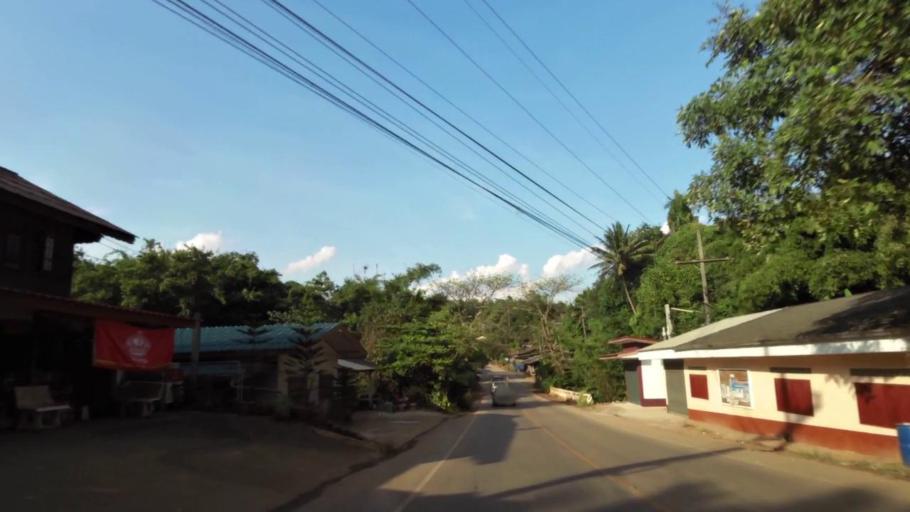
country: TH
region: Chiang Rai
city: Khun Tan
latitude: 19.8656
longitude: 100.3990
